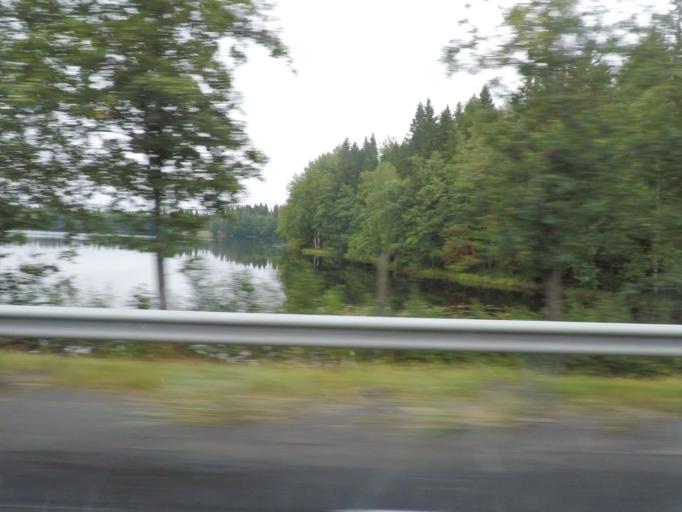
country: FI
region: Northern Savo
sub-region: Kuopio
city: Kuopio
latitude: 62.9262
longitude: 27.6756
